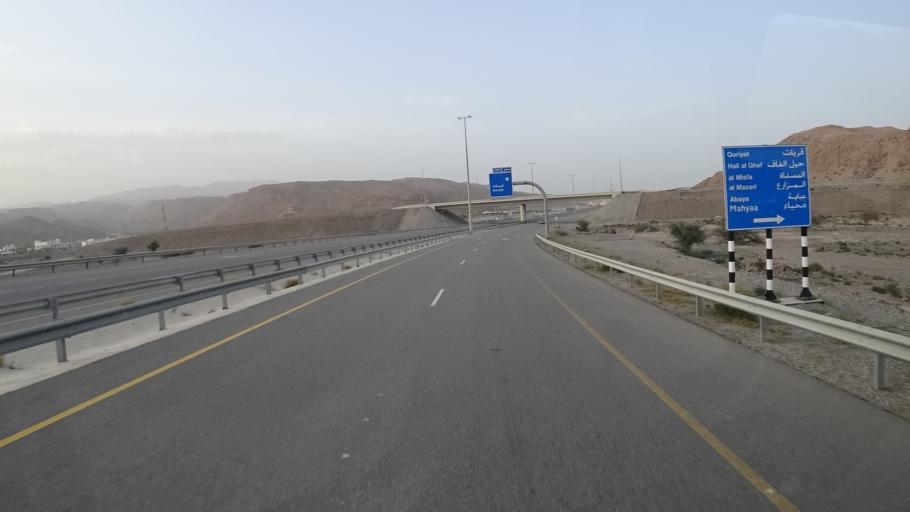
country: OM
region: Muhafazat Masqat
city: Muscat
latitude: 23.1991
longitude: 58.8804
